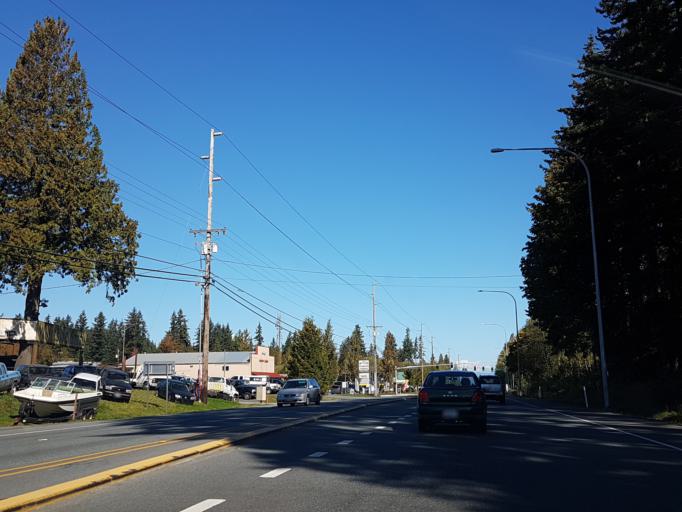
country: US
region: Washington
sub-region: Snohomish County
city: Clearview
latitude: 47.8358
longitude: -122.1249
